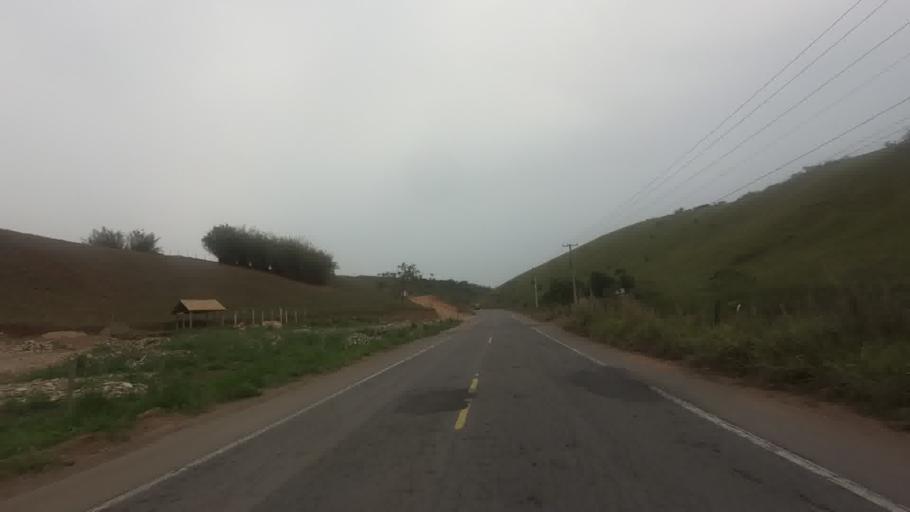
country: BR
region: Rio de Janeiro
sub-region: Santo Antonio De Padua
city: Santo Antonio de Padua
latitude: -21.6045
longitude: -42.2456
